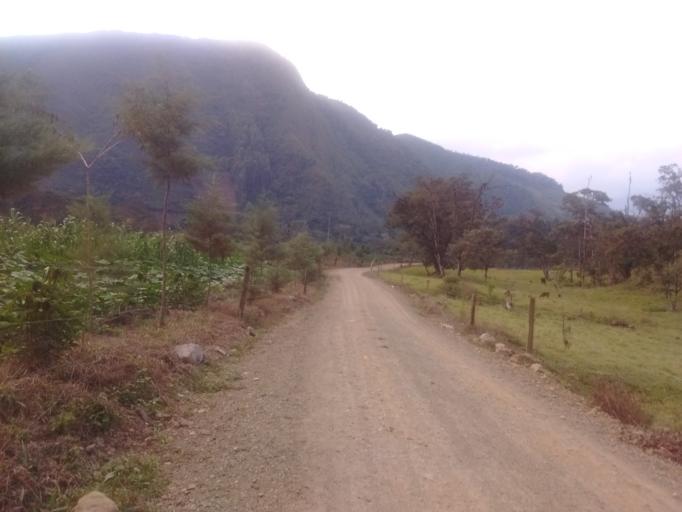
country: PE
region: Pasco
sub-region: Provincia de Oxapampa
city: Oxapampa
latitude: -10.5427
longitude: -75.4295
